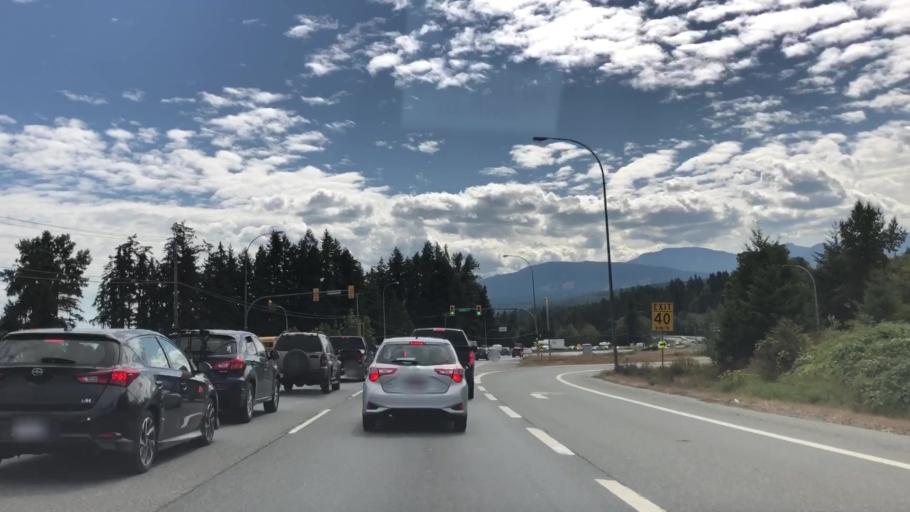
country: CA
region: British Columbia
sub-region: Cowichan Valley Regional District
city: Ladysmith
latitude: 49.0355
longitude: -123.8632
